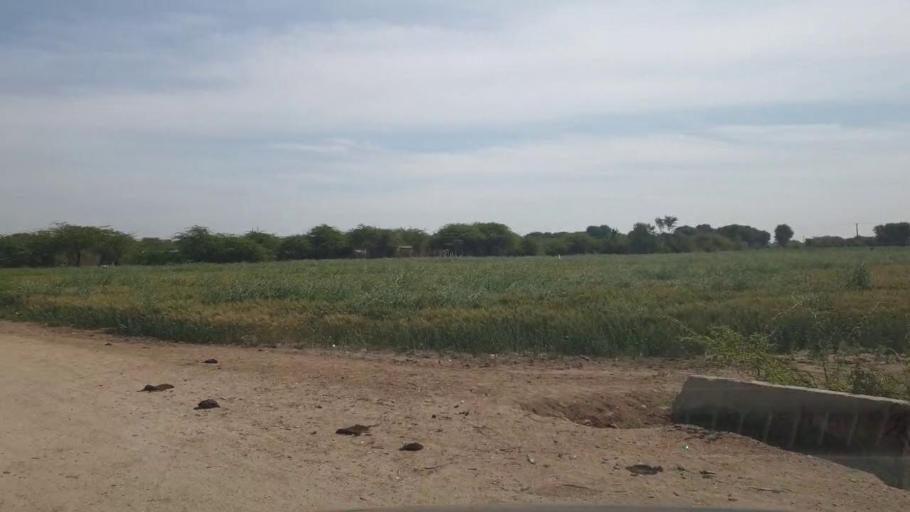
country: PK
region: Sindh
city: Kunri
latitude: 25.3097
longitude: 69.5744
